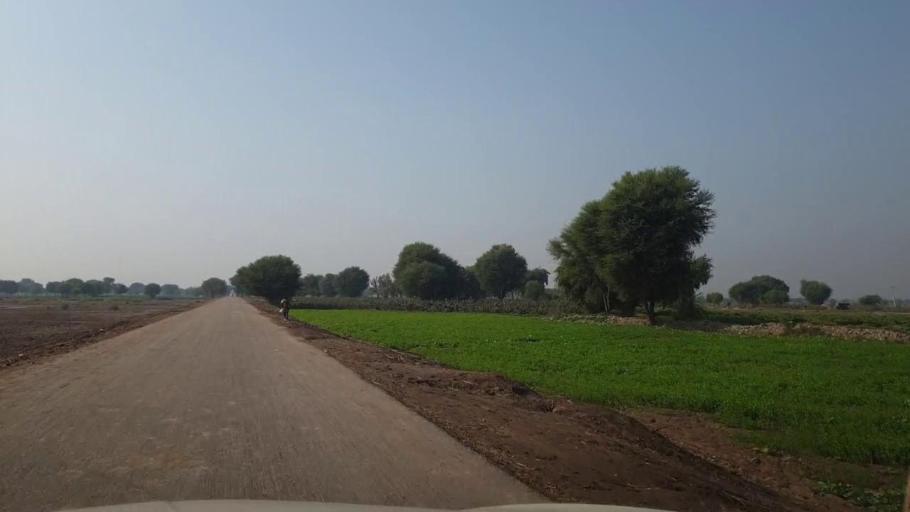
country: PK
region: Sindh
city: Bhan
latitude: 26.5220
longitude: 67.8078
